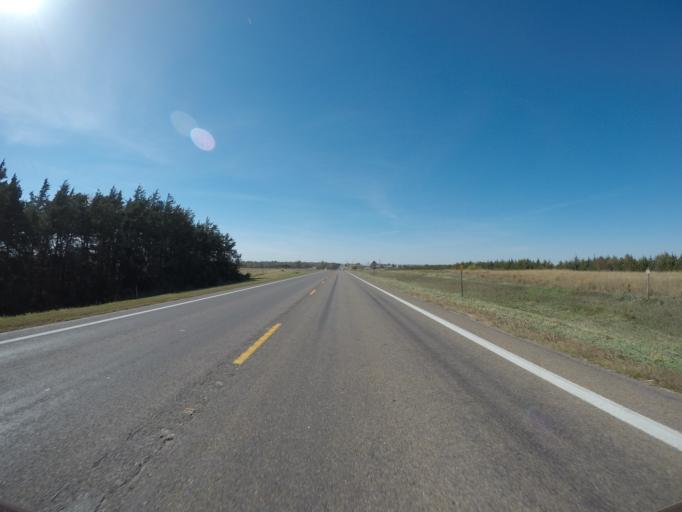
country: US
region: Kansas
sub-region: Smith County
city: Smith Center
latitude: 39.7710
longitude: -99.0190
